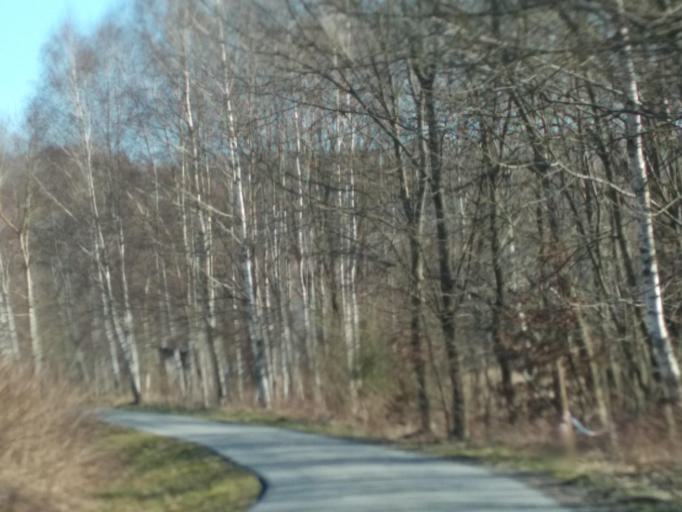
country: PL
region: Subcarpathian Voivodeship
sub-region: Powiat ropczycko-sedziszowski
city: Iwierzyce
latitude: 49.9515
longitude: 21.7441
